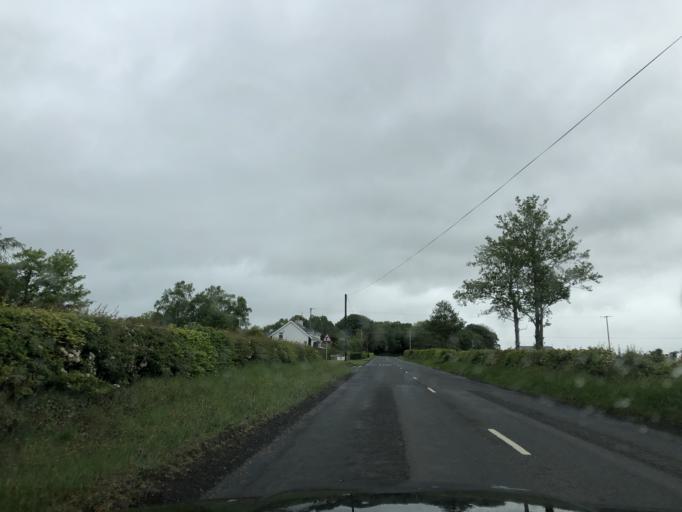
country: GB
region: Northern Ireland
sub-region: Ballymoney District
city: Ballymoney
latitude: 55.1176
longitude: -6.4897
